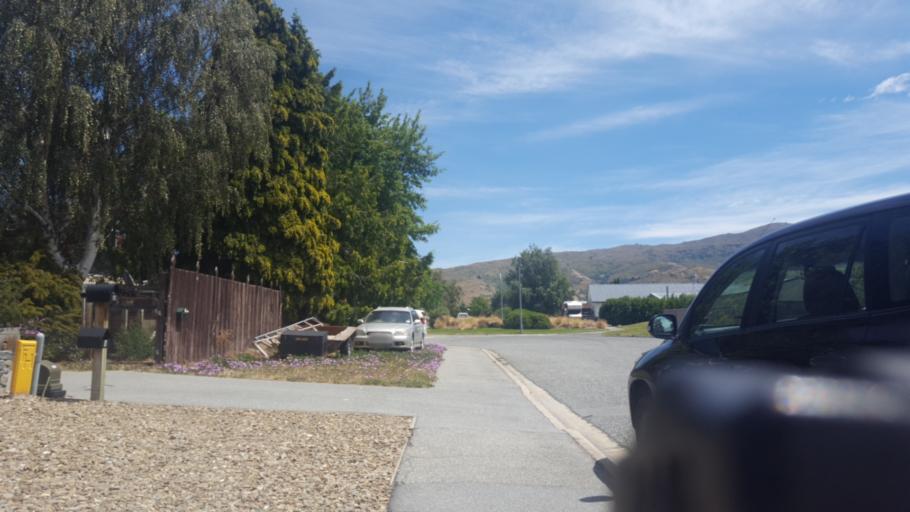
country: NZ
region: Otago
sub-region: Queenstown-Lakes District
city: Wanaka
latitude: -45.0435
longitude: 169.1996
